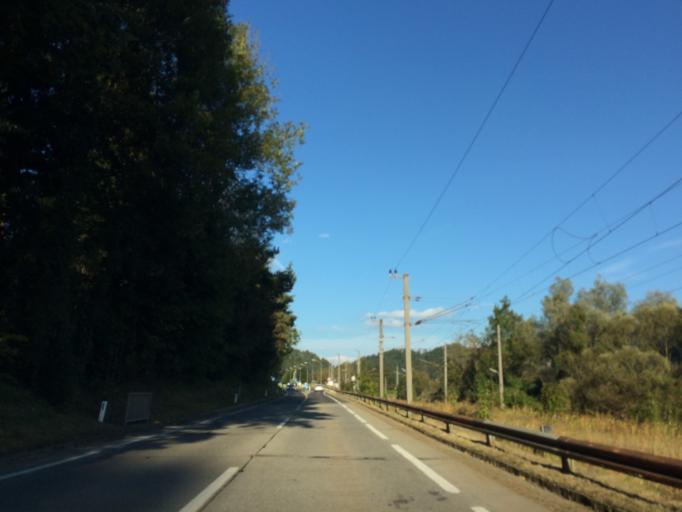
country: AT
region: Styria
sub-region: Politischer Bezirk Leoben
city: Leoben
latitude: 47.3579
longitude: 15.0575
